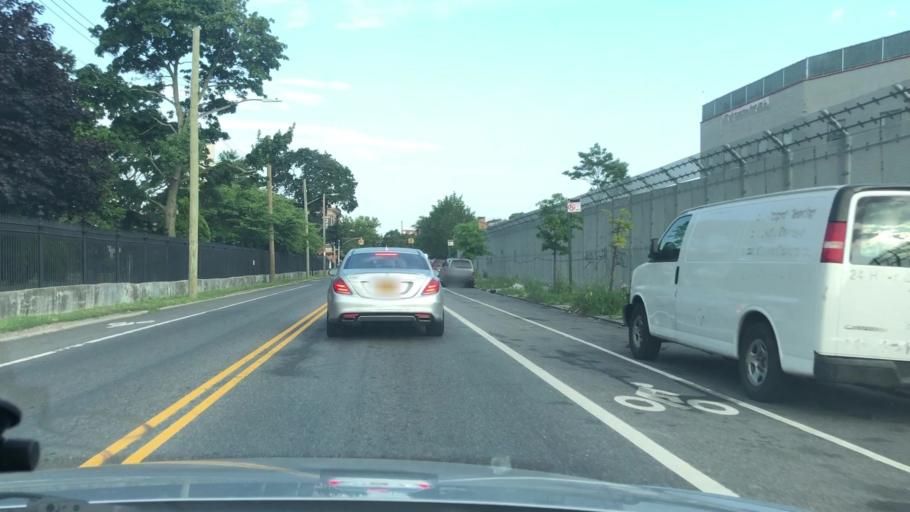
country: US
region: New York
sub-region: Kings County
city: Brooklyn
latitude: 40.6449
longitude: -73.9904
